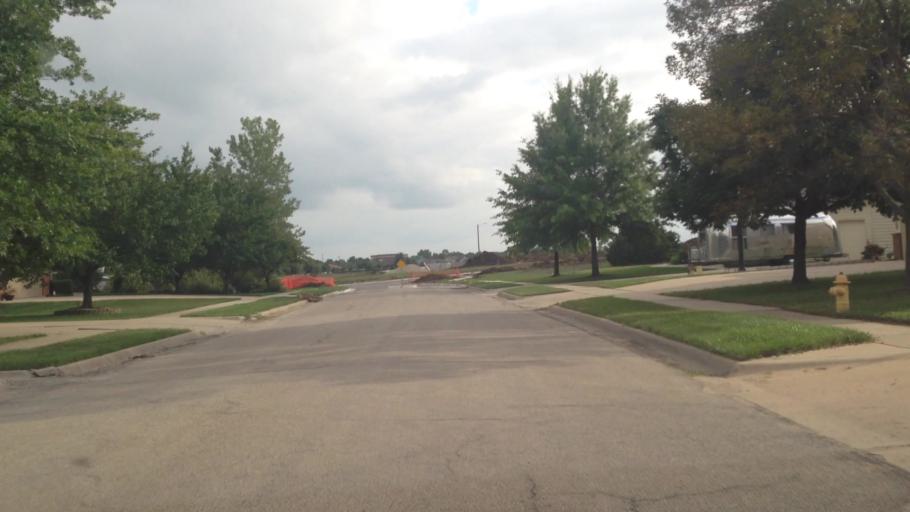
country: US
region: Kansas
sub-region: Douglas County
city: Lawrence
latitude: 38.9671
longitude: -95.3116
